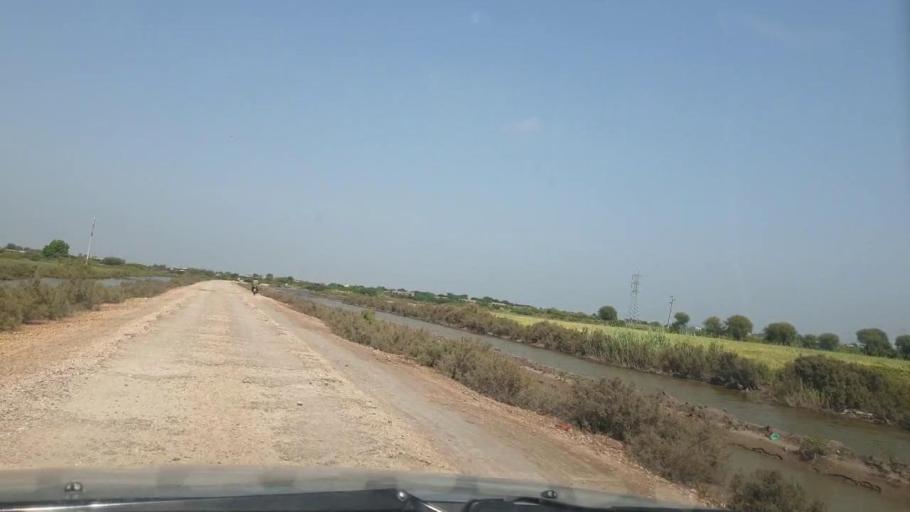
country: PK
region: Sindh
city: Tando Ghulam Ali
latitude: 25.0677
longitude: 68.8011
